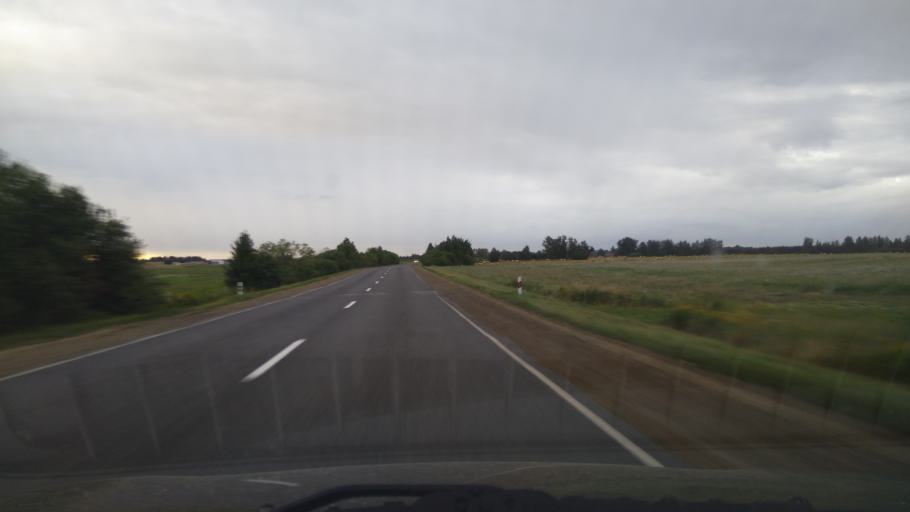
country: BY
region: Brest
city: Byaroza
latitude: 52.4443
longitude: 24.9738
